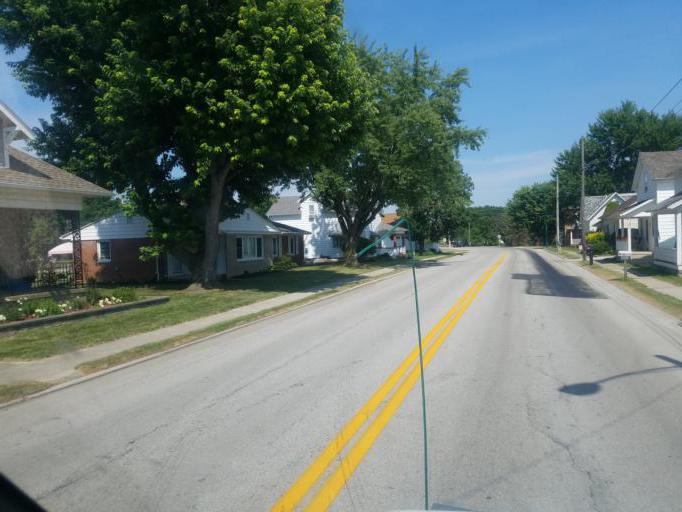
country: US
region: Ohio
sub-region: Auglaize County
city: New Bremen
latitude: 40.4955
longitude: -84.3153
